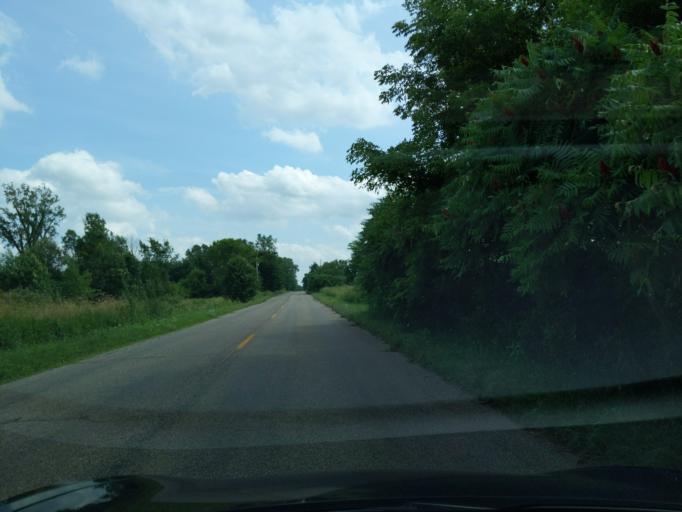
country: US
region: Michigan
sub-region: Eaton County
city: Eaton Rapids
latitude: 42.5469
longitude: -84.6019
